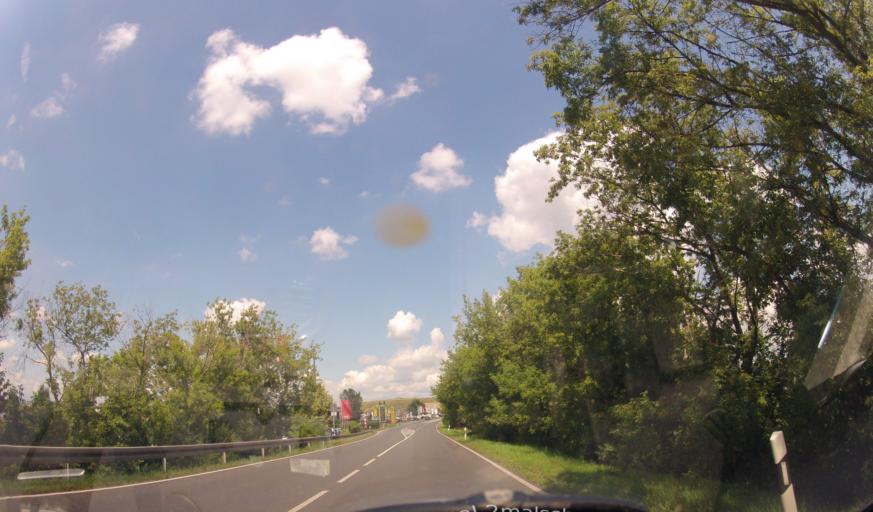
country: DE
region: Saxony
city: Zinna
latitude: 51.5545
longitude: 12.9661
